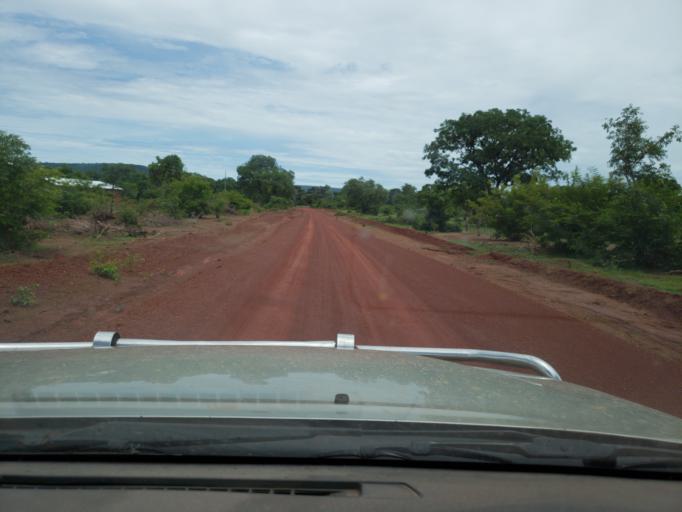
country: ML
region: Sikasso
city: Sikasso
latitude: 11.6772
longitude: -6.3330
